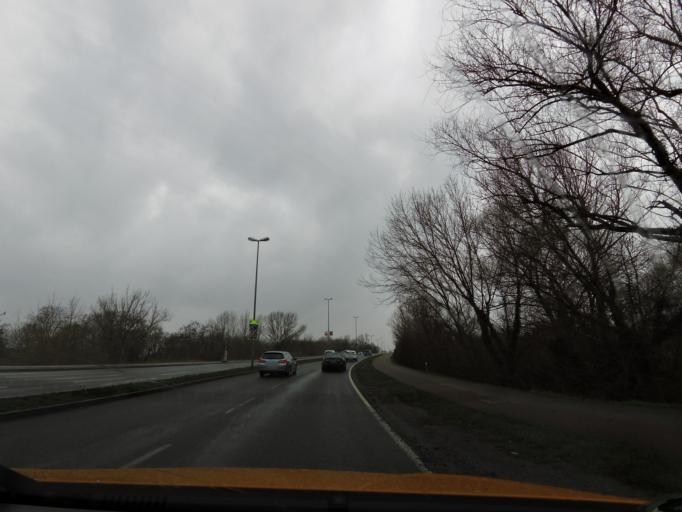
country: DE
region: Brandenburg
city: Brandenburg an der Havel
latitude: 52.4033
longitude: 12.5396
